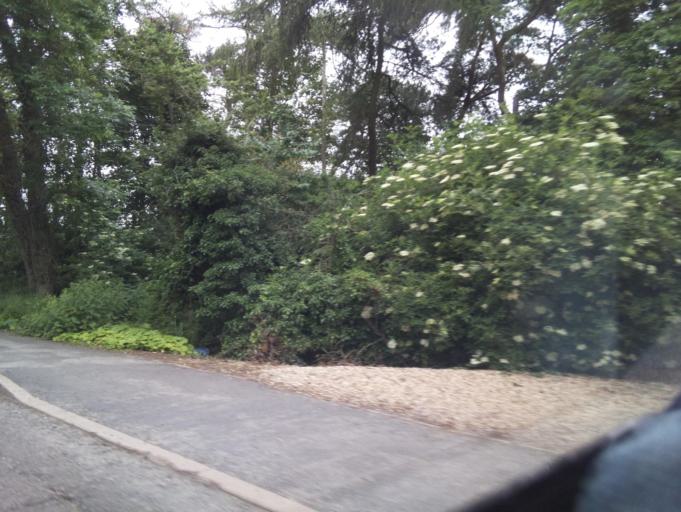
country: GB
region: England
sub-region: District of Rutland
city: Edith Weston
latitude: 52.6396
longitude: -0.6274
